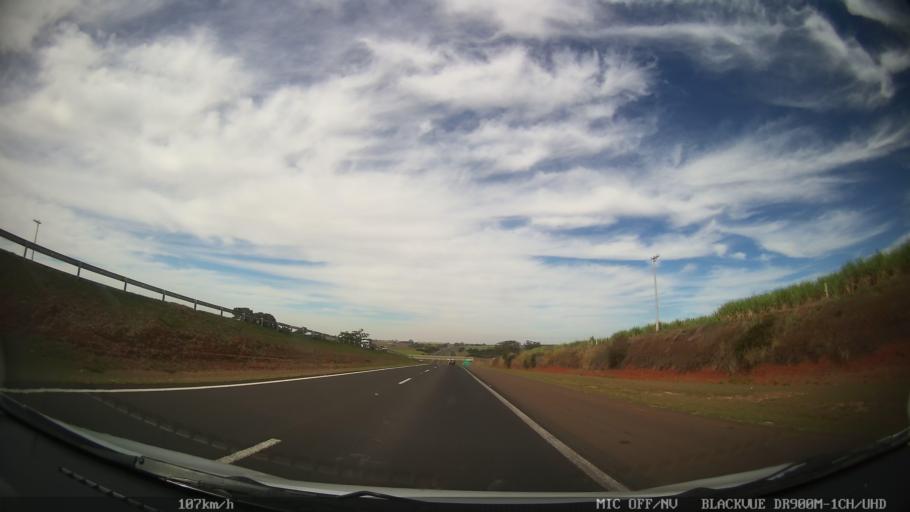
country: BR
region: Sao Paulo
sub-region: Taquaritinga
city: Taquaritinga
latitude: -21.5136
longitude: -48.5437
